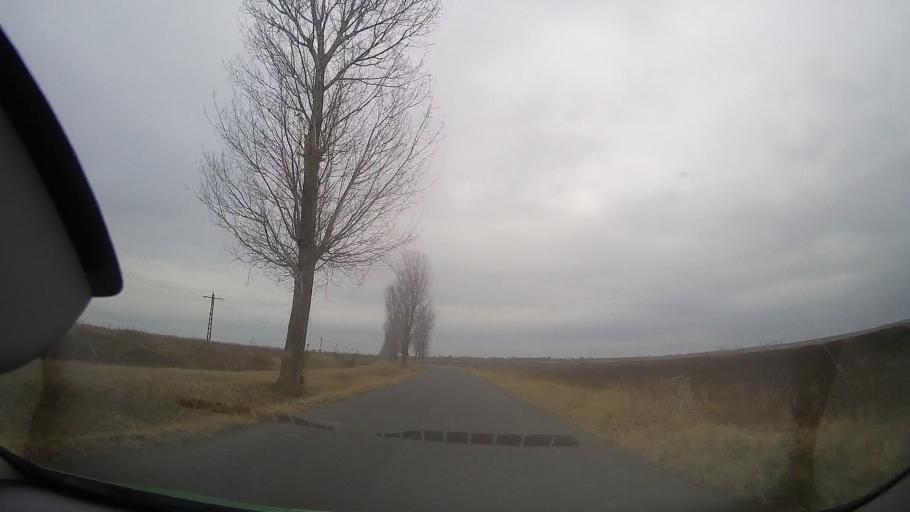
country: RO
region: Braila
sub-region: Comuna Rosiori
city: Rosiori
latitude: 44.8156
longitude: 27.3643
